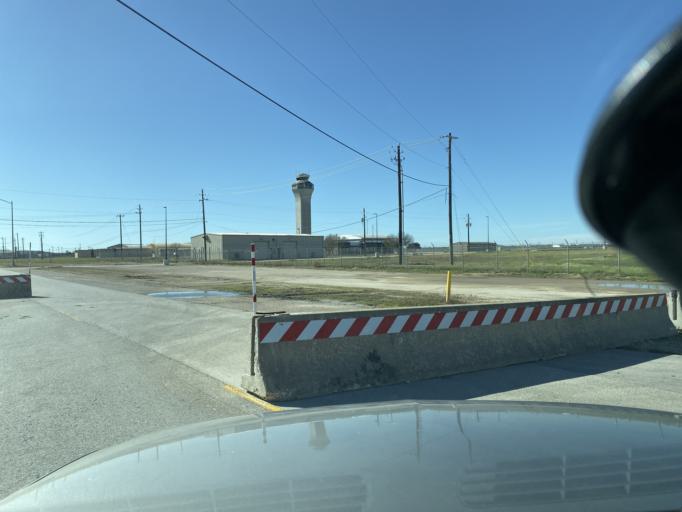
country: US
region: Texas
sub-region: Travis County
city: Hornsby Bend
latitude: 30.1969
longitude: -97.6610
